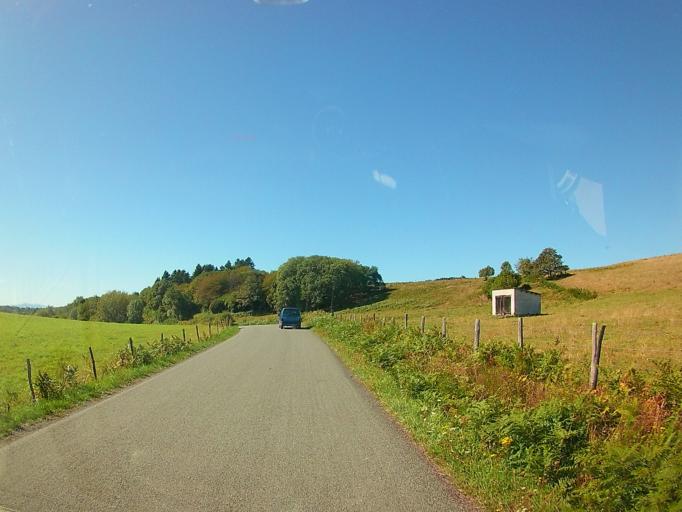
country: FR
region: Auvergne
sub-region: Departement du Puy-de-Dome
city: Manzat
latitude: 45.9214
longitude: 2.9480
